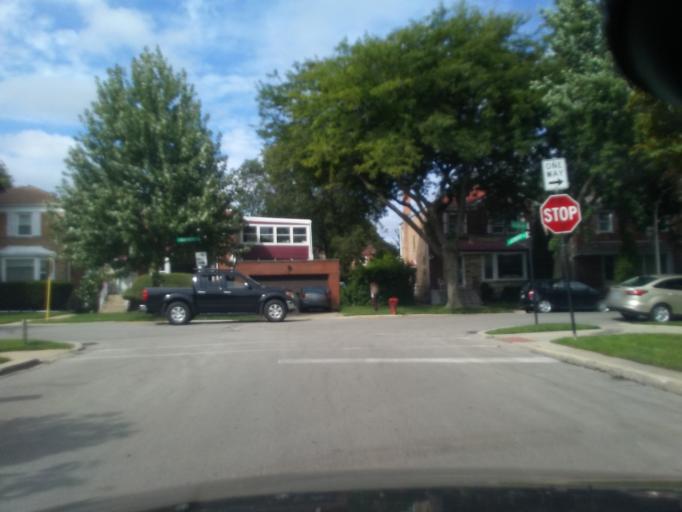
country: US
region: Illinois
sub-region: Cook County
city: Lincolnwood
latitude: 41.9922
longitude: -87.7041
